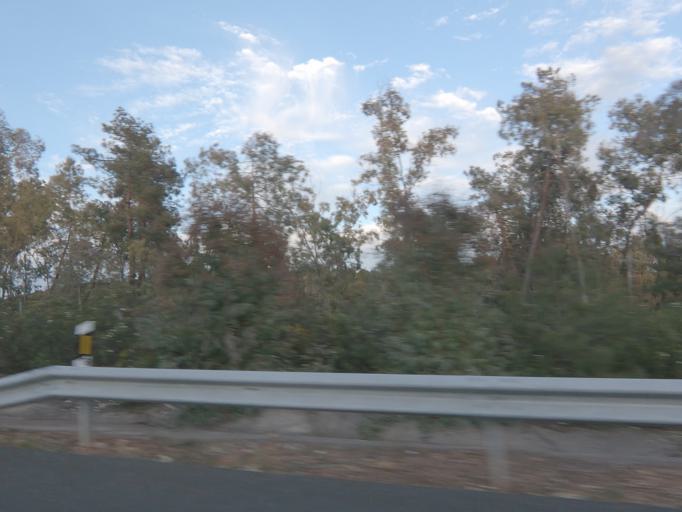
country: ES
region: Extremadura
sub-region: Provincia de Caceres
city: Alcuescar
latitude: 39.1527
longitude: -6.2746
